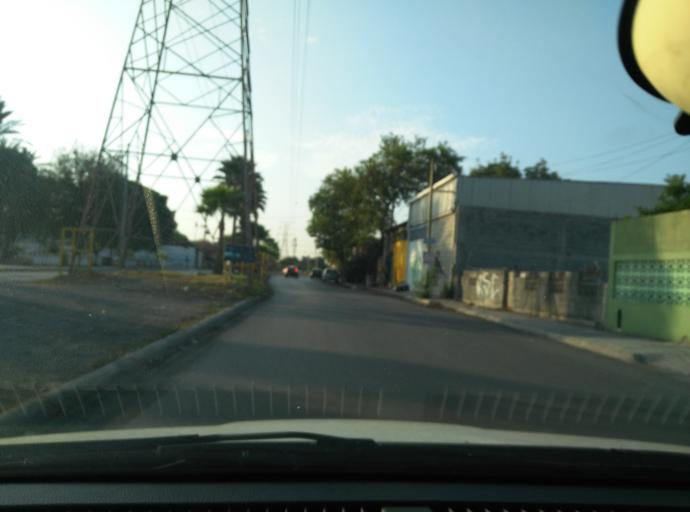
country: MX
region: Nuevo Leon
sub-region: San Nicolas de los Garza
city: San Nicolas de los Garza
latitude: 25.7582
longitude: -100.2502
